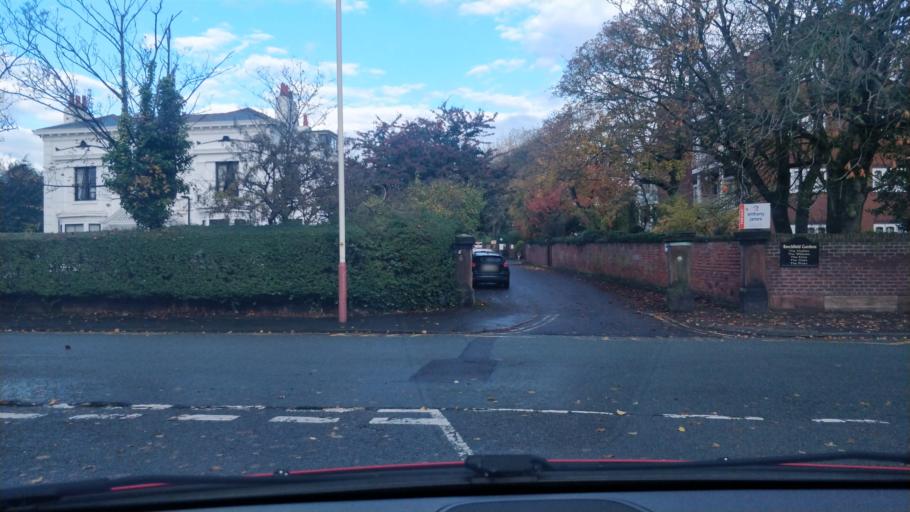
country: GB
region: England
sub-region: Sefton
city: Southport
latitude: 53.6423
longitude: -3.0160
